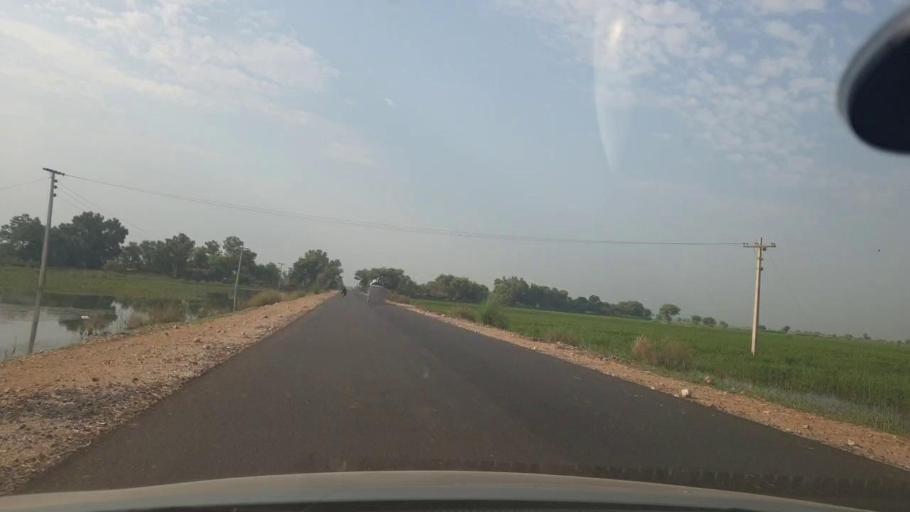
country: PK
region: Sindh
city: Jacobabad
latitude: 28.1134
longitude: 68.3268
